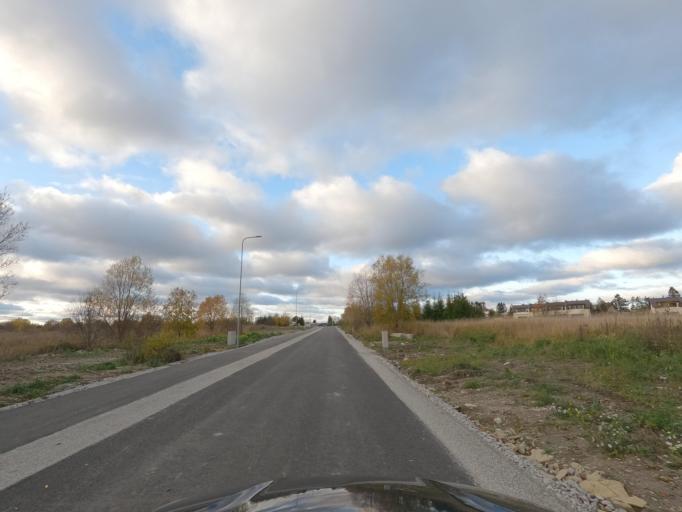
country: EE
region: Harju
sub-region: Rae vald
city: Jueri
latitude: 59.3701
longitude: 24.8462
